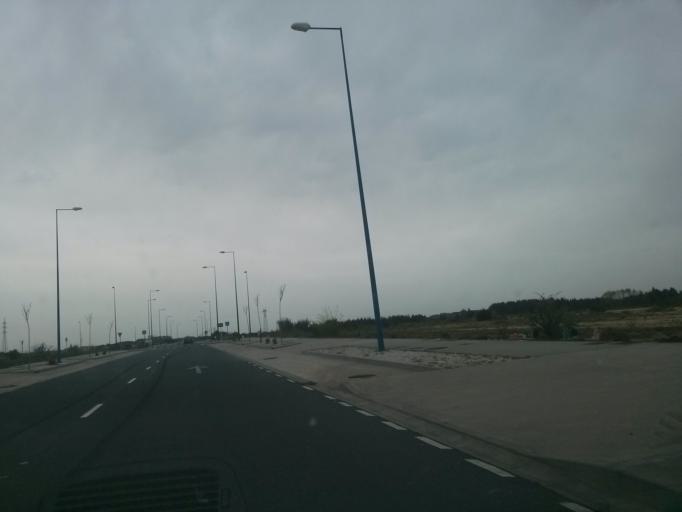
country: ES
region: Galicia
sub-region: Provincia de Lugo
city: Lugo
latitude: 43.0432
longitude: -7.5493
